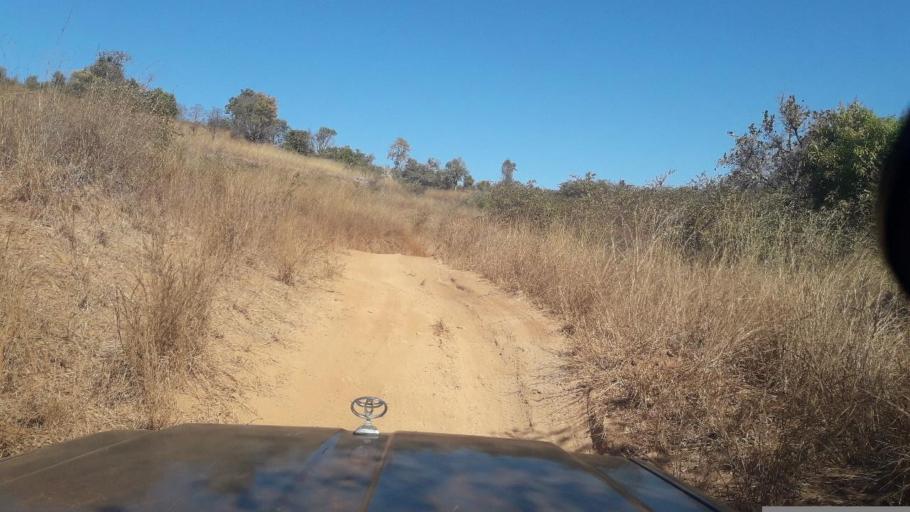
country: MG
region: Boeny
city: Sitampiky
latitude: -16.3118
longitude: 45.6303
